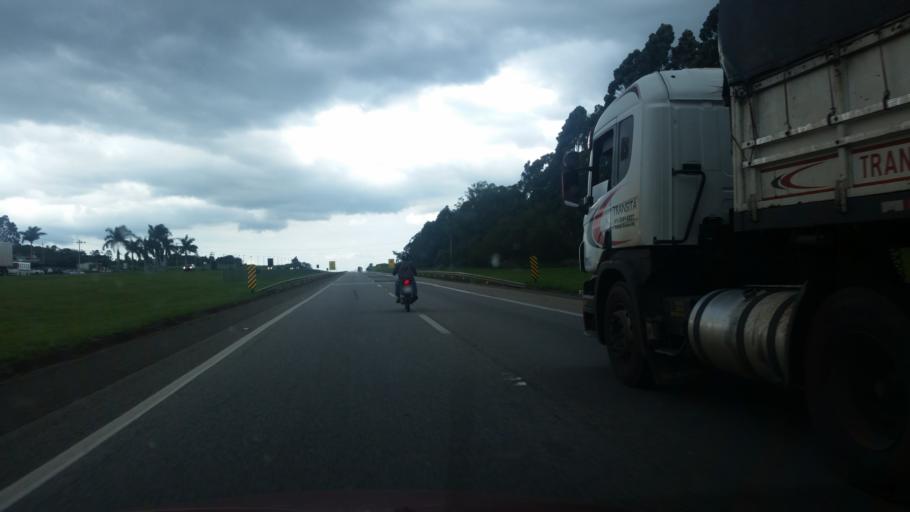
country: BR
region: Sao Paulo
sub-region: Porto Feliz
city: Porto Feliz
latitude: -23.3353
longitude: -47.5487
